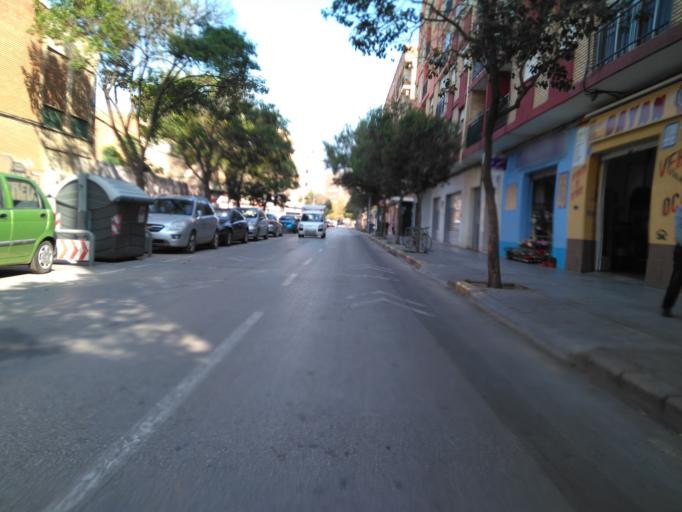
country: ES
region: Valencia
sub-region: Provincia de Valencia
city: Tavernes Blanques
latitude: 39.4923
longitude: -0.3883
